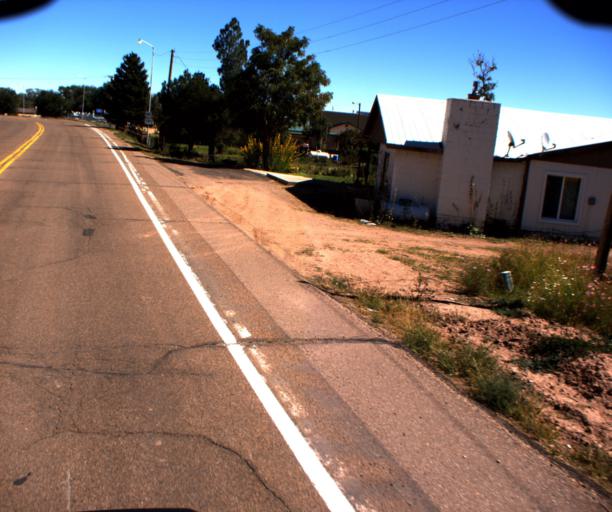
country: US
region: Arizona
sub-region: Apache County
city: Saint Johns
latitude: 34.4993
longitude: -109.3655
